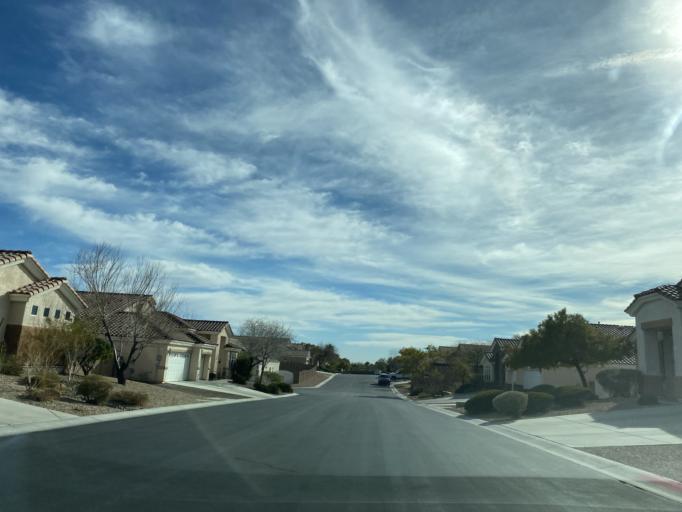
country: US
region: Nevada
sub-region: Clark County
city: Summerlin South
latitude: 36.2742
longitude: -115.3259
